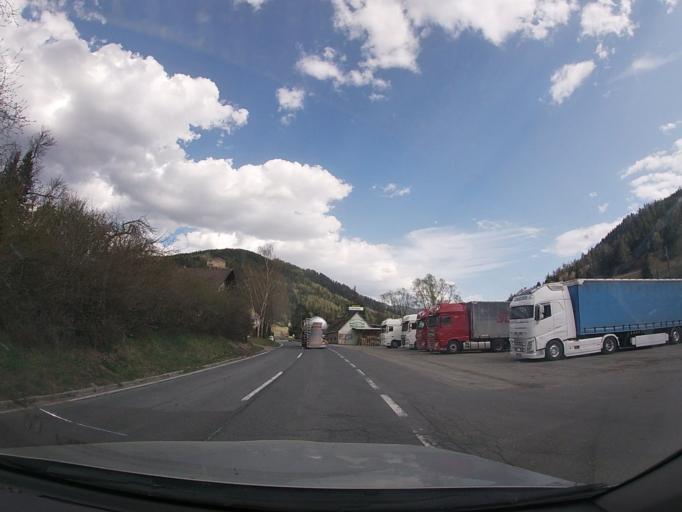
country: AT
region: Styria
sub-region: Politischer Bezirk Murau
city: Sankt Lorenzen bei Scheifling
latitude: 47.1397
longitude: 14.4250
